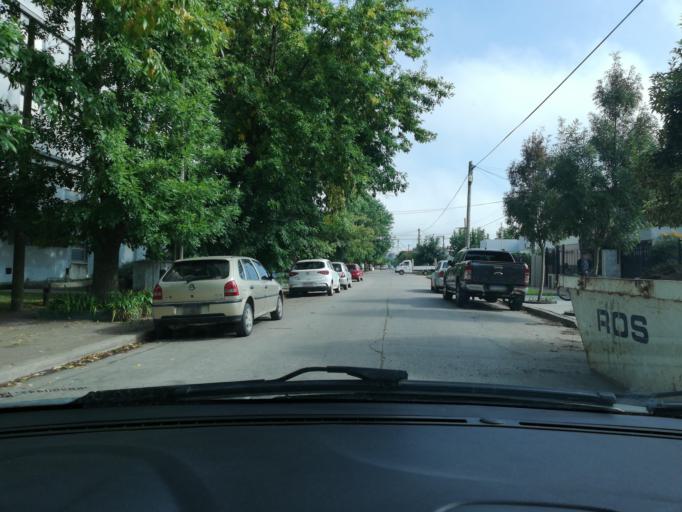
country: AR
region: Buenos Aires
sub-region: Partido de Balcarce
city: Balcarce
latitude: -37.8392
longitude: -58.2626
